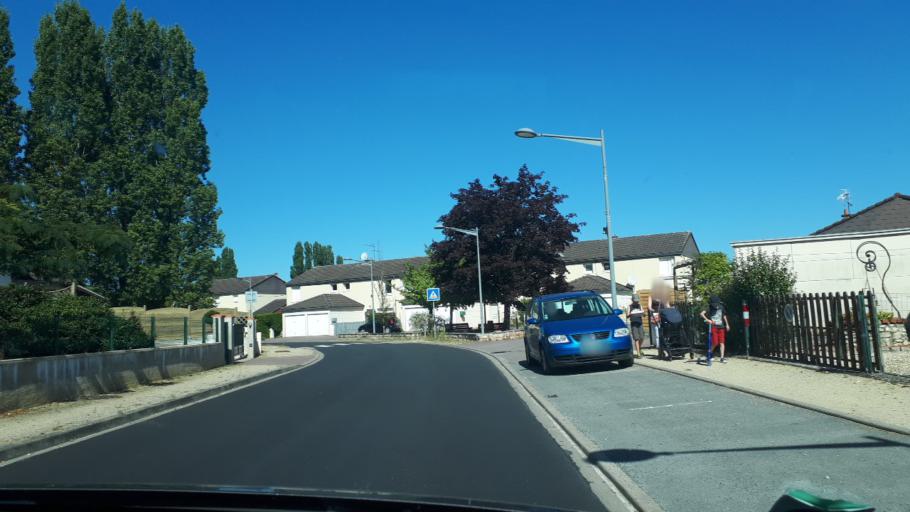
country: FR
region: Centre
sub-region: Departement du Loiret
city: Coullons
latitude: 47.6235
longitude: 2.4942
